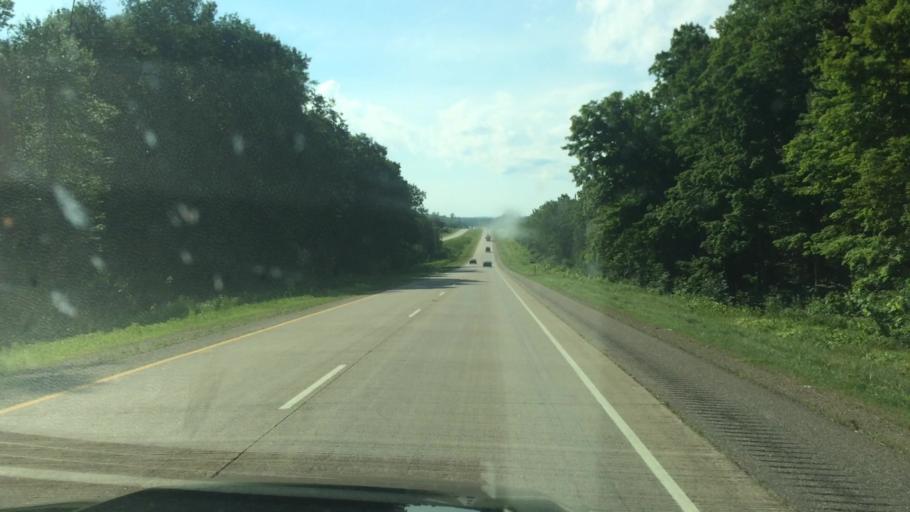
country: US
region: Wisconsin
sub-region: Shawano County
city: Wittenberg
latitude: 44.8175
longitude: -89.0513
